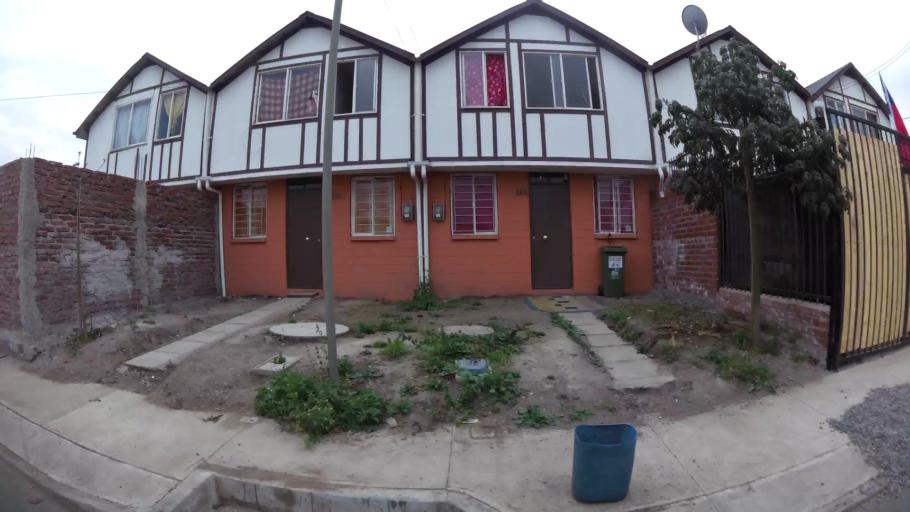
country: CL
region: Santiago Metropolitan
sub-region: Provincia de Chacabuco
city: Chicureo Abajo
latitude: -33.1976
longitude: -70.6675
